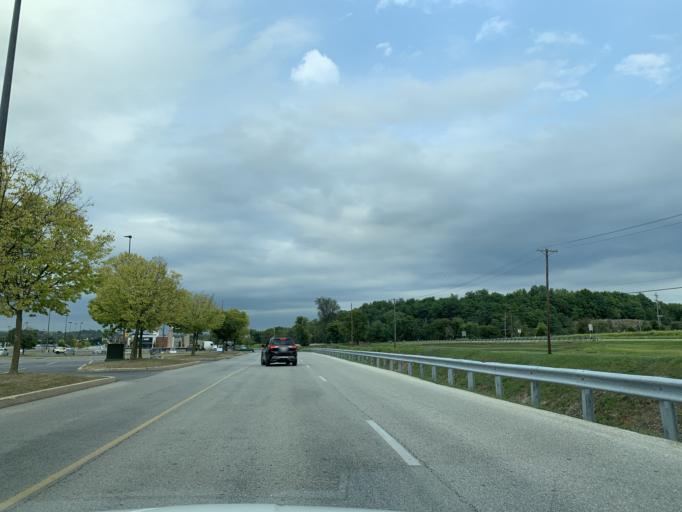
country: US
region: Pennsylvania
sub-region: York County
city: West York
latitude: 39.9670
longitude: -76.7718
